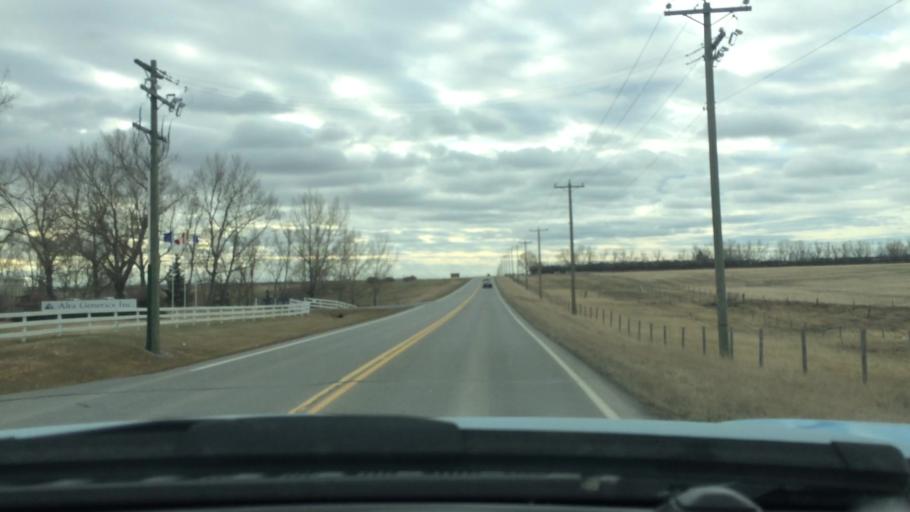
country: CA
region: Alberta
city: Airdrie
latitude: 51.2320
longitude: -114.0250
